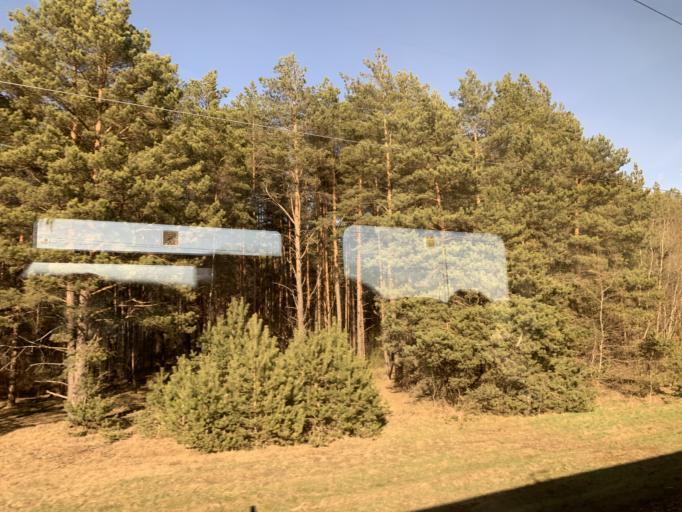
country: BY
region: Grodnenskaya
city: Astravyets
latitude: 54.5759
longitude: 25.9411
